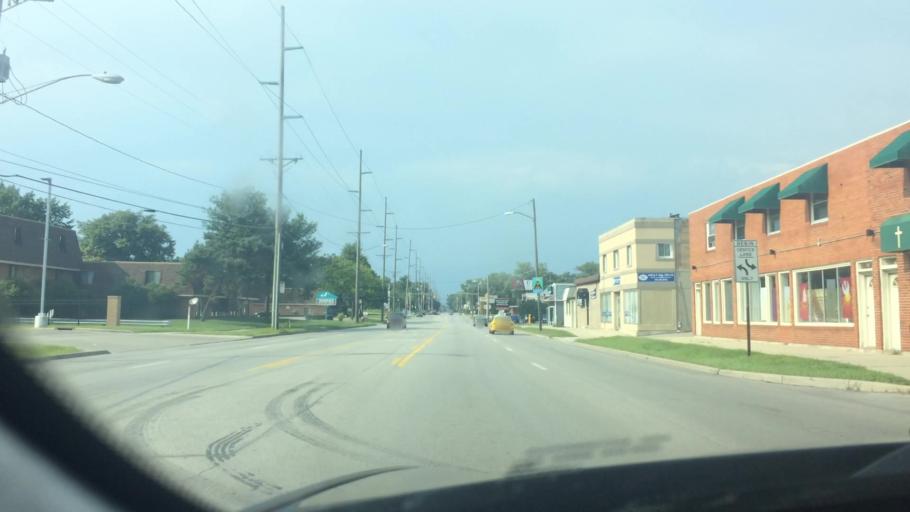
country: US
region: Ohio
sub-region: Lucas County
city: Ottawa Hills
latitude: 41.6930
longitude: -83.6232
